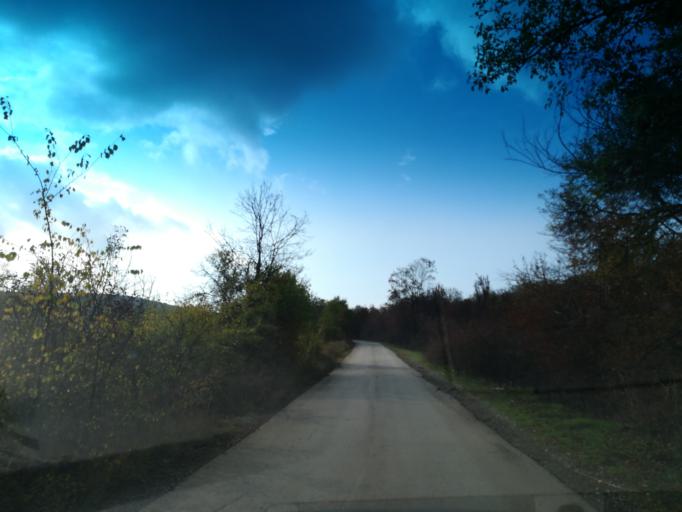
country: BG
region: Stara Zagora
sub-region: Obshtina Nikolaevo
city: Elkhovo
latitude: 42.3344
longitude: 25.4049
